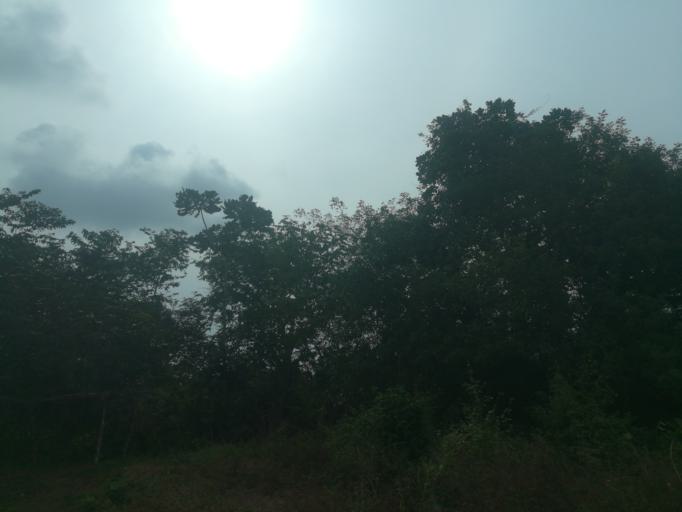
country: NG
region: Ogun
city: Ayetoro
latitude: 7.2935
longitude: 3.0788
